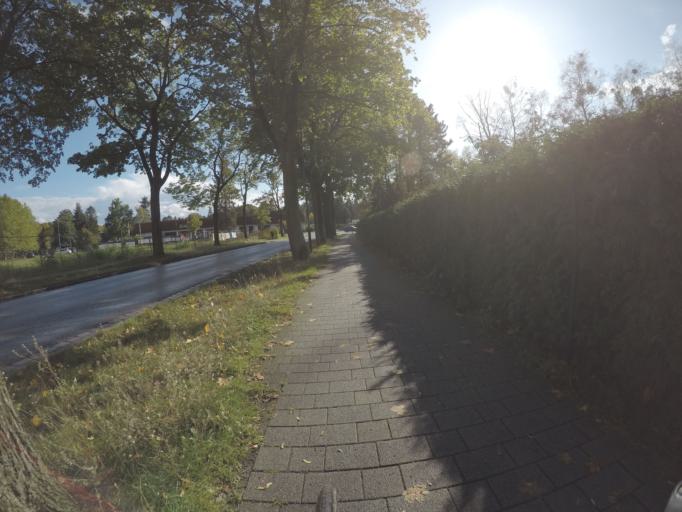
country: DE
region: Brandenburg
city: Petershagen
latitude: 52.5281
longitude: 13.7909
